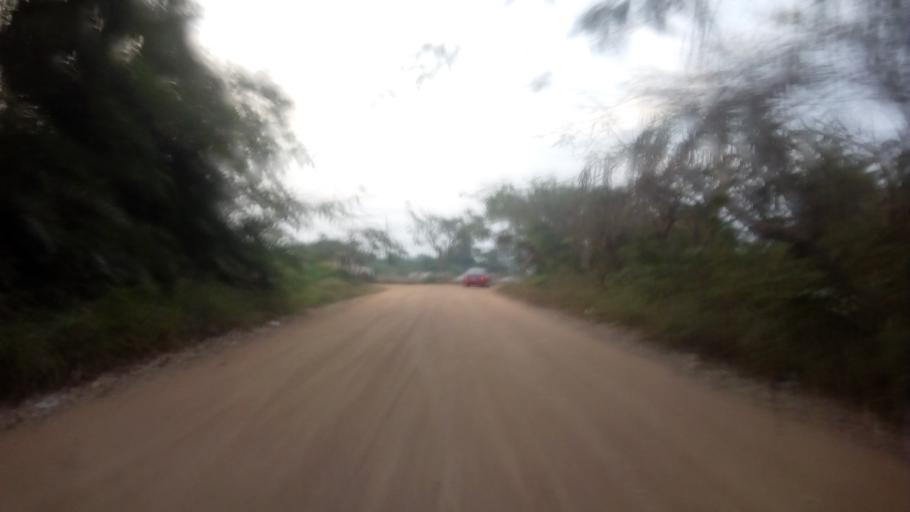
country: GH
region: Central
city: Cape Coast
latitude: 5.1177
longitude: -1.2742
